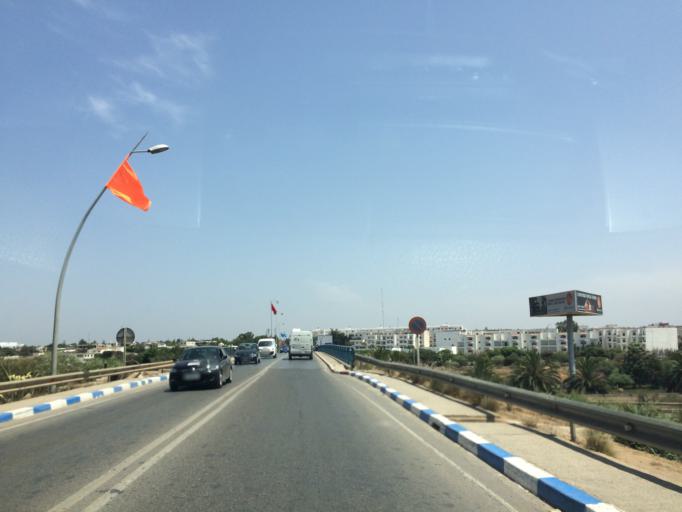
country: MA
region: Rabat-Sale-Zemmour-Zaer
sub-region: Skhirate-Temara
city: Temara
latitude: 33.9332
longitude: -6.9377
